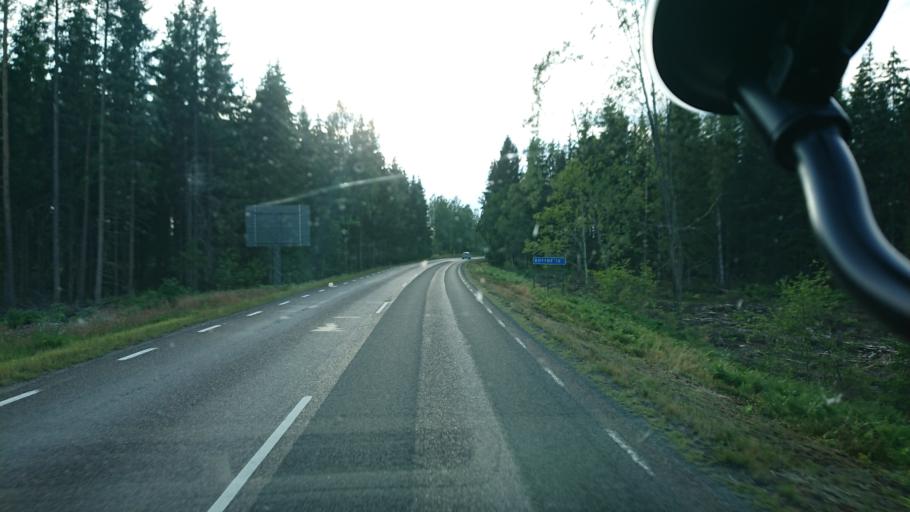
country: SE
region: Kronoberg
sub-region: Vaxjo Kommun
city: Braas
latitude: 57.0177
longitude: 15.0490
